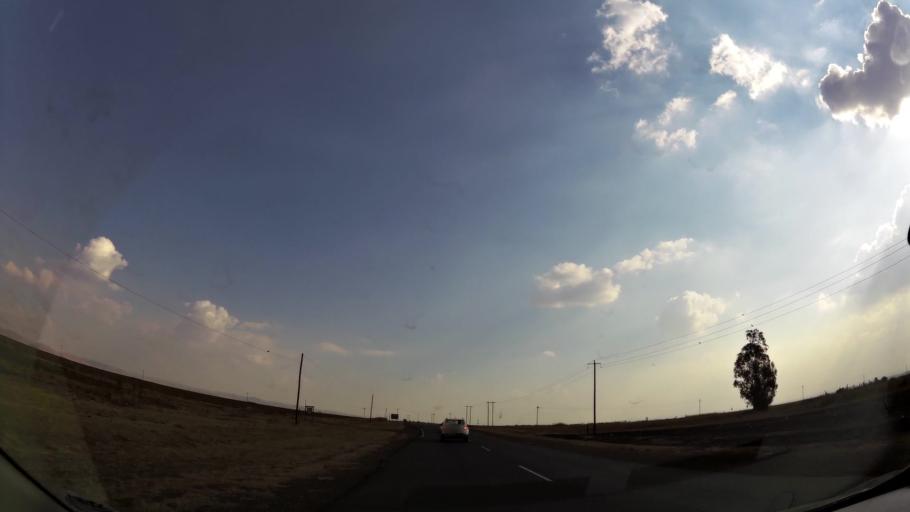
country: ZA
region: Gauteng
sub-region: Sedibeng District Municipality
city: Heidelberg
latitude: -26.3880
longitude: 28.2986
